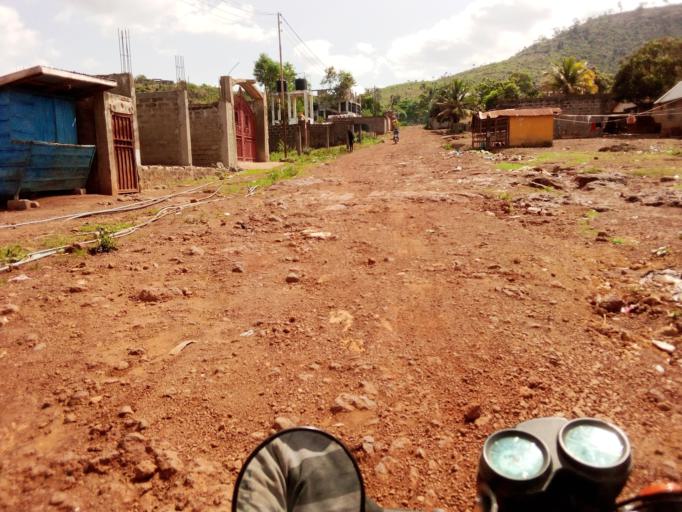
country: SL
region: Western Area
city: Waterloo
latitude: 8.3388
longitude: -13.0770
